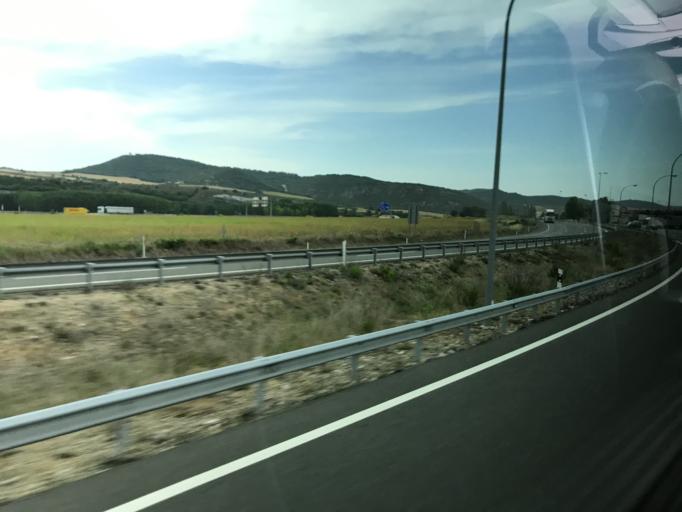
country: ES
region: Basque Country
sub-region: Provincia de Alava
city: Arminon
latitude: 42.7144
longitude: -2.8668
